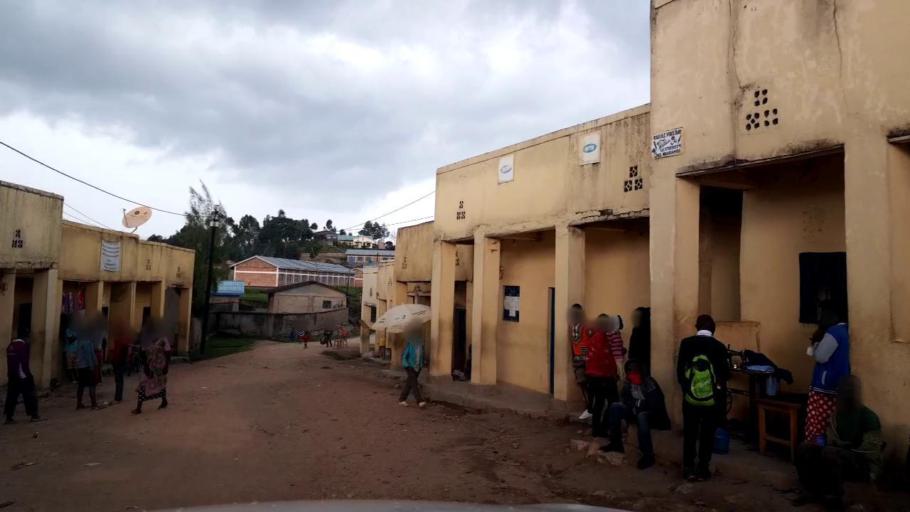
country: RW
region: Southern Province
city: Gitarama
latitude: -1.8710
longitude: 29.5916
